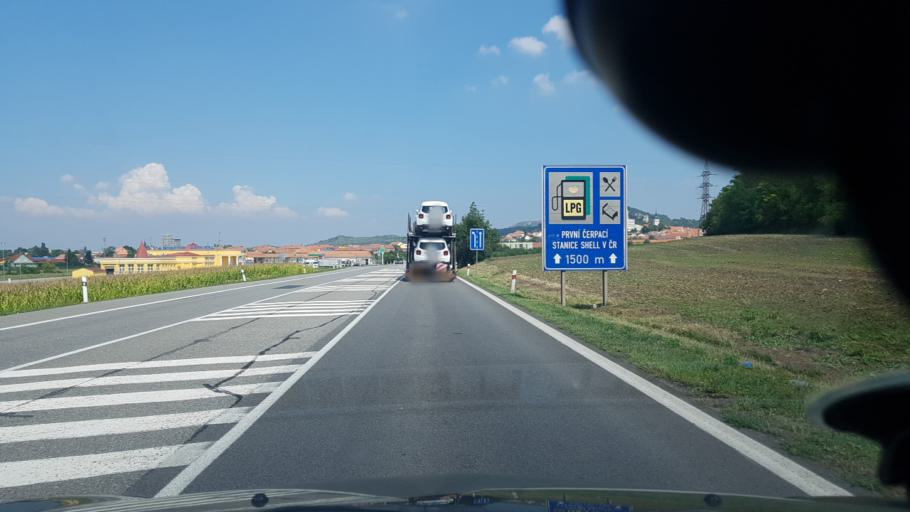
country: CZ
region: South Moravian
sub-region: Okres Breclav
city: Mikulov
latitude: 48.7947
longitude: 16.6337
